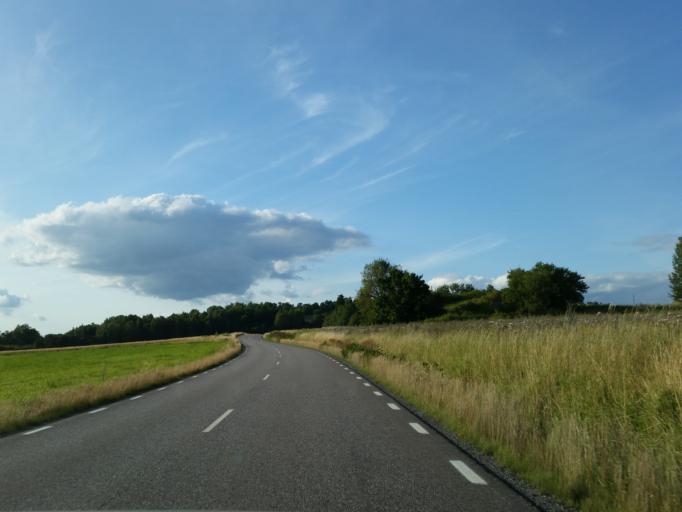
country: SE
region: Soedermanland
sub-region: Gnesta Kommun
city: Gnesta
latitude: 59.0243
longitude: 17.3603
